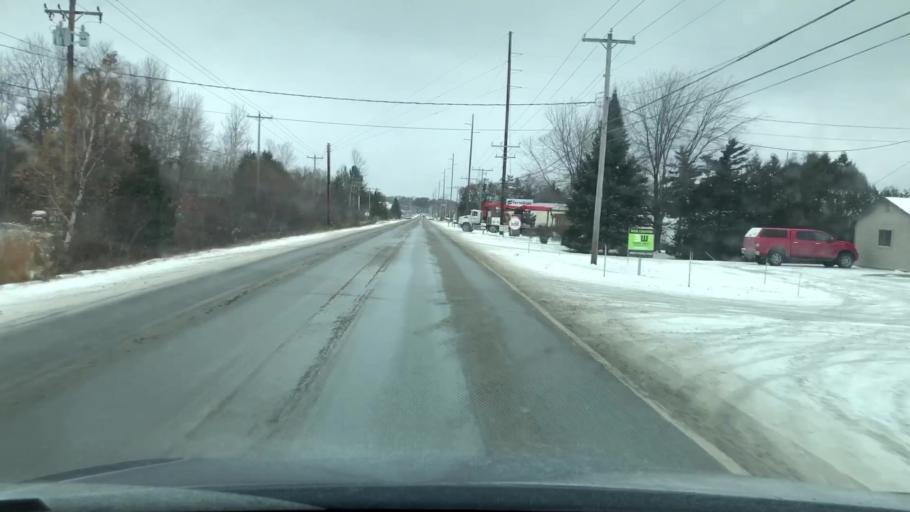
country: US
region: Michigan
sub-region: Grand Traverse County
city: Traverse City
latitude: 44.7192
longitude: -85.6258
